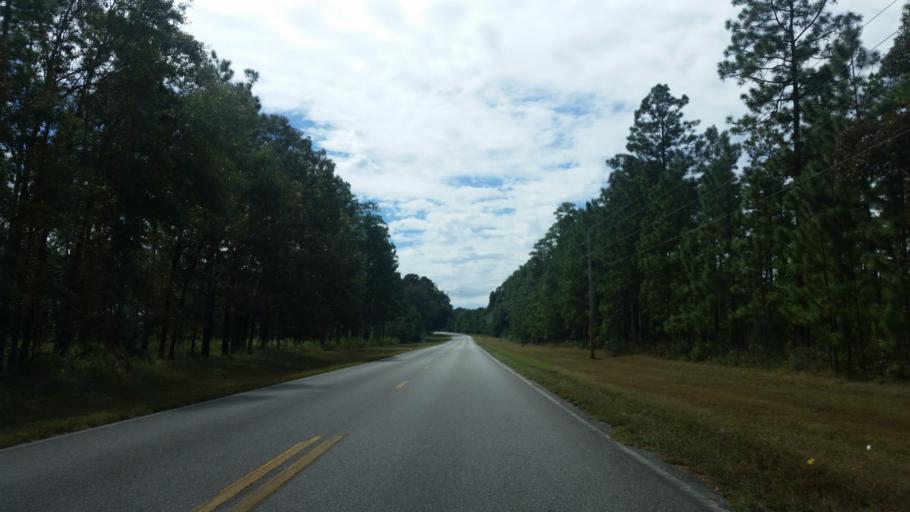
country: US
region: Florida
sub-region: Santa Rosa County
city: Point Baker
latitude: 30.8062
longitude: -86.9357
